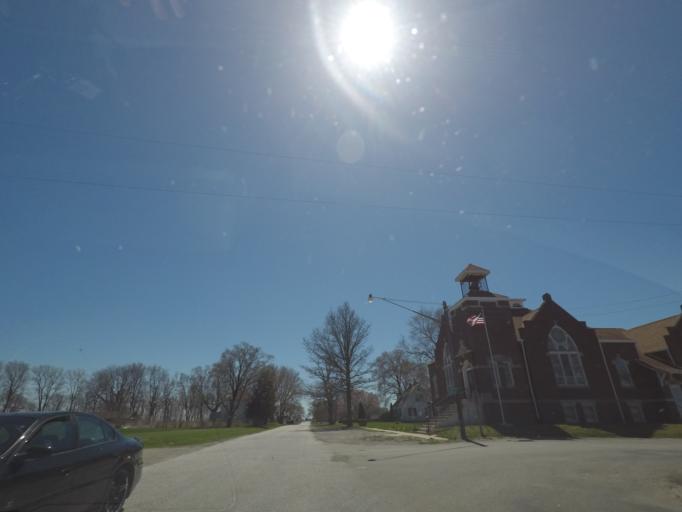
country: US
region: Illinois
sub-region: Logan County
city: Mount Pulaski
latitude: 40.0557
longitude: -89.1825
